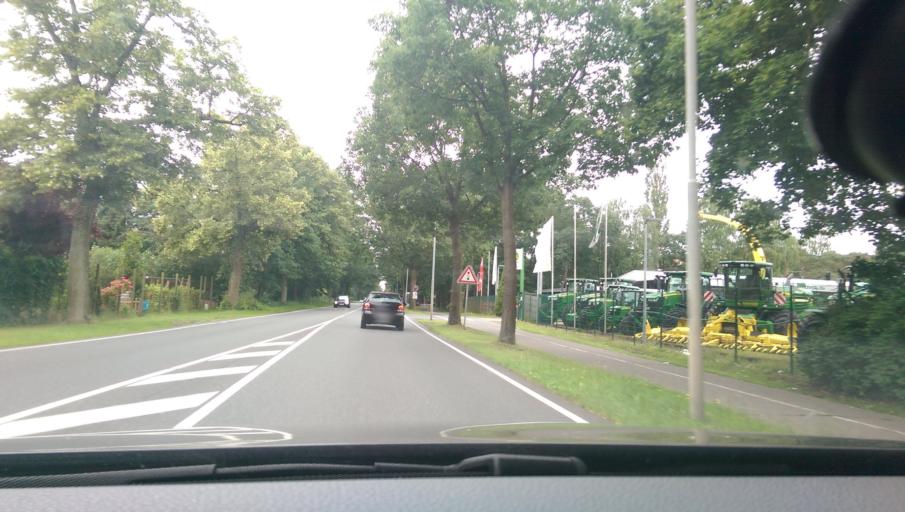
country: DE
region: Lower Saxony
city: Rotenburg
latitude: 53.0977
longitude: 9.3783
